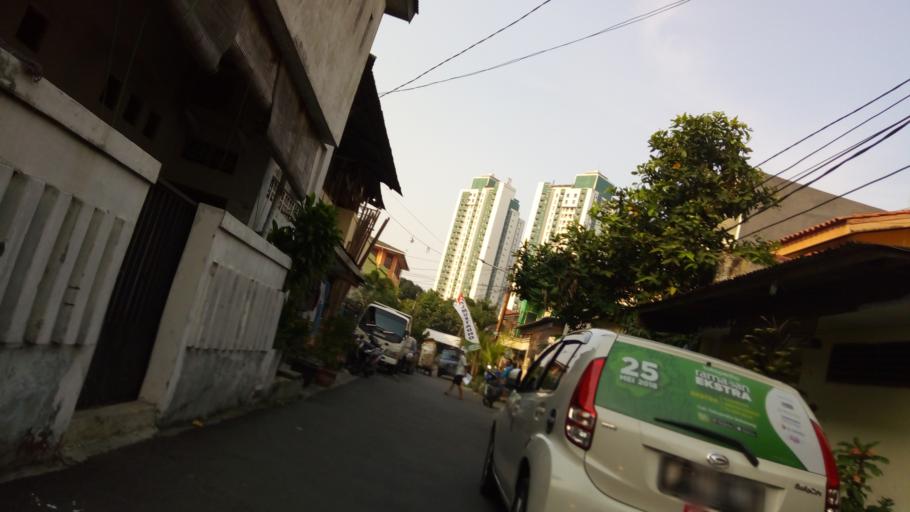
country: ID
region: Jakarta Raya
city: Jakarta
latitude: -6.1966
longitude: 106.8531
